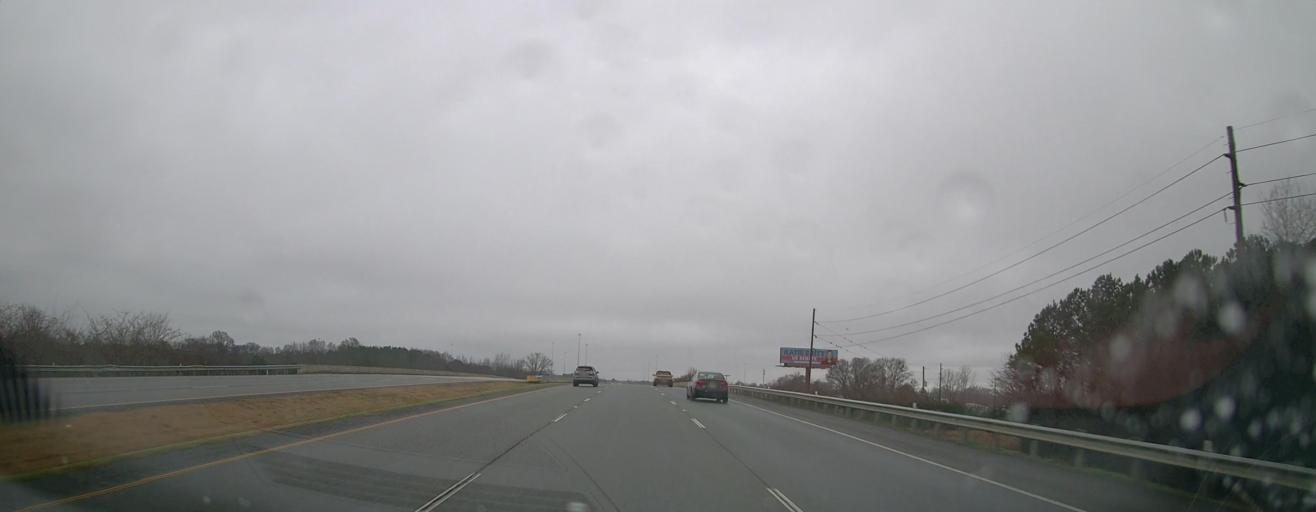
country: US
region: Alabama
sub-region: Morgan County
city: Decatur
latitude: 34.6105
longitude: -87.0313
